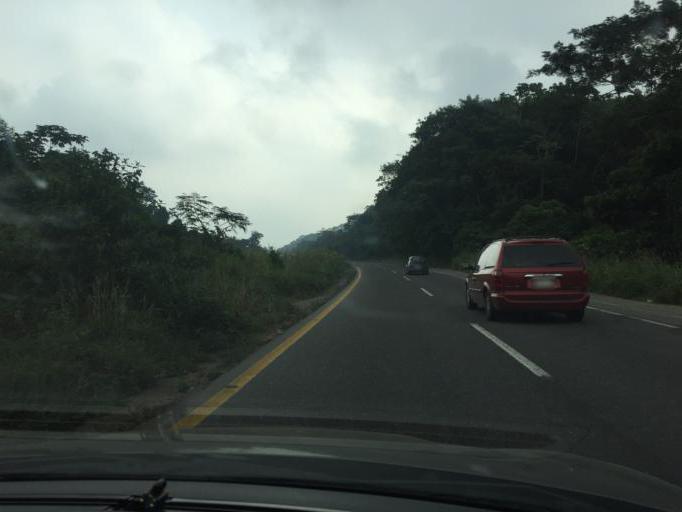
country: MX
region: Veracruz
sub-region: Moloacan
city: Tlacuilolapan
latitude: 18.0743
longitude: -94.2654
